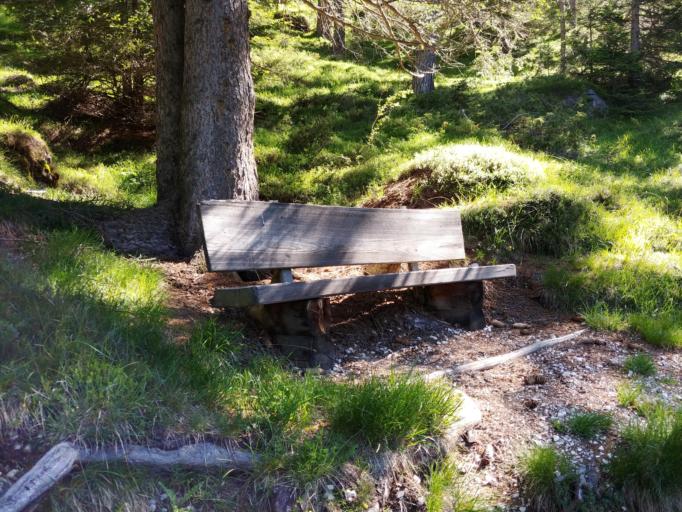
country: IT
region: Trentino-Alto Adige
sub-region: Bolzano
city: Selva
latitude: 46.5638
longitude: 11.7559
